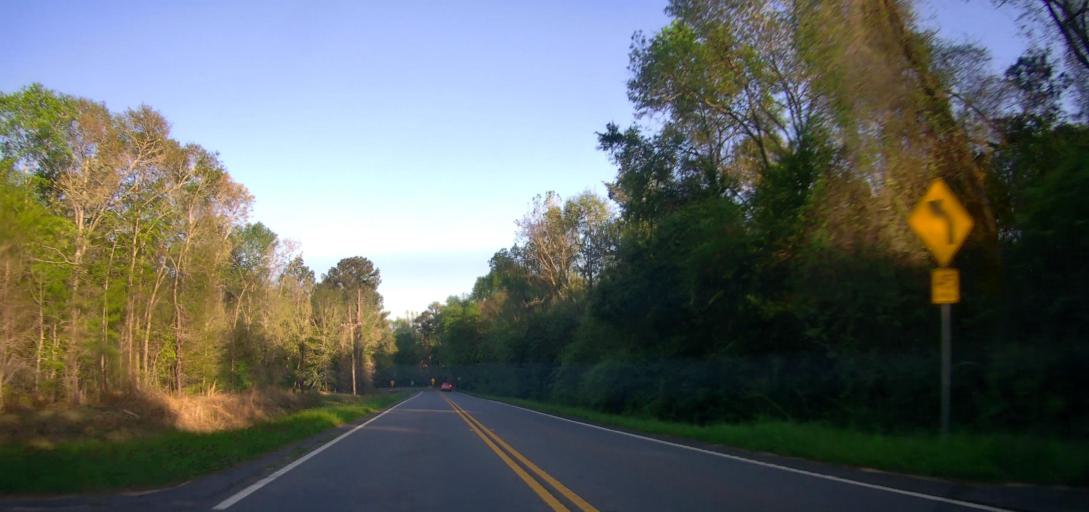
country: US
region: Georgia
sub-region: Schley County
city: Ellaville
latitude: 32.3175
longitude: -84.2572
